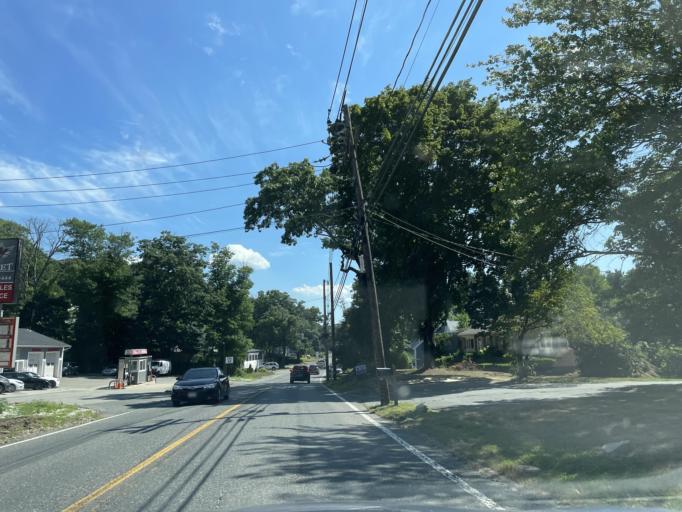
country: US
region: Massachusetts
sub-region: Middlesex County
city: Holliston
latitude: 42.2306
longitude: -71.4312
